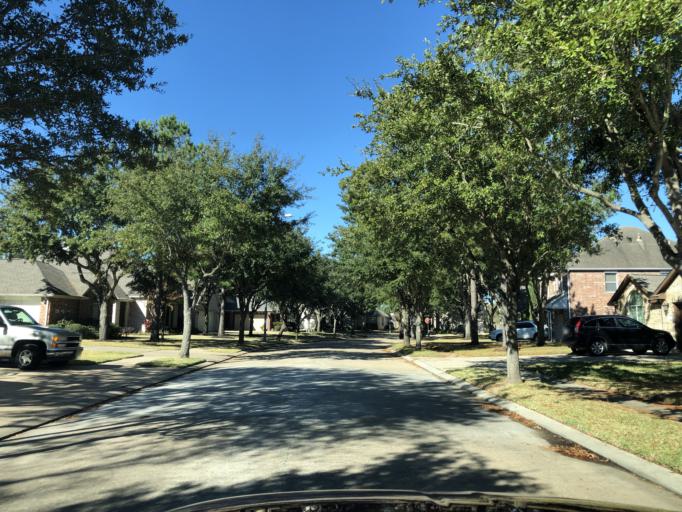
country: US
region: Texas
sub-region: Harris County
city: Oak Cliff Place
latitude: 29.9426
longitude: -95.6634
